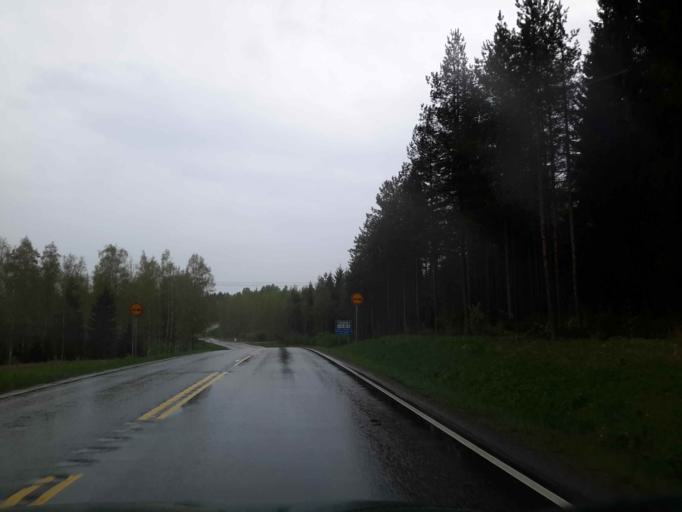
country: FI
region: Uusimaa
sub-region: Helsinki
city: Vihti
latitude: 60.3844
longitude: 24.5136
